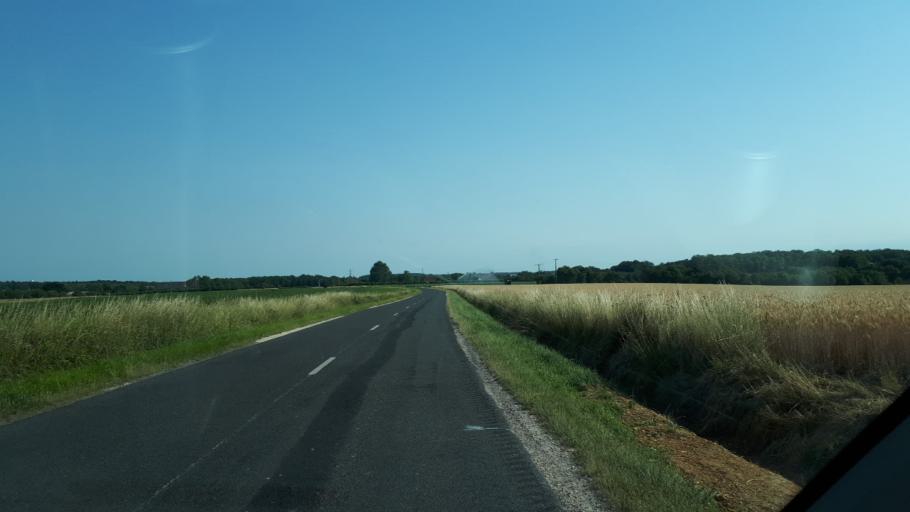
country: FR
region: Centre
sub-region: Departement du Loir-et-Cher
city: La Ville-aux-Clercs
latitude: 47.9468
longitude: 1.0806
